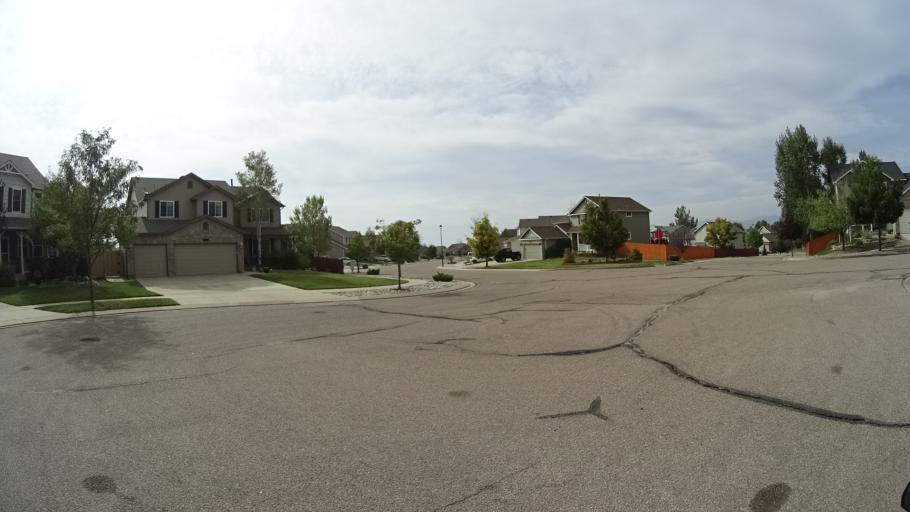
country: US
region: Colorado
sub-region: El Paso County
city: Cimarron Hills
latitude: 38.9173
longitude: -104.7068
